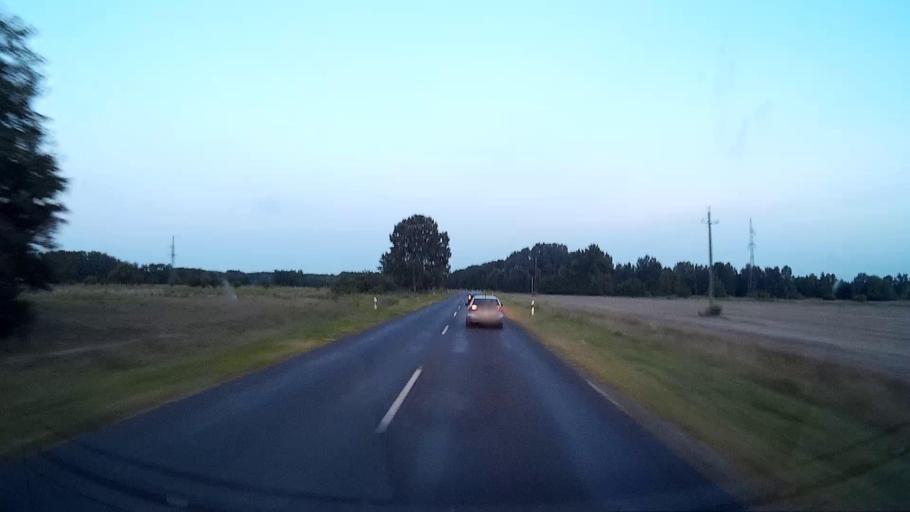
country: HU
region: Pest
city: Cegledbercel
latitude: 47.2061
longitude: 19.6911
